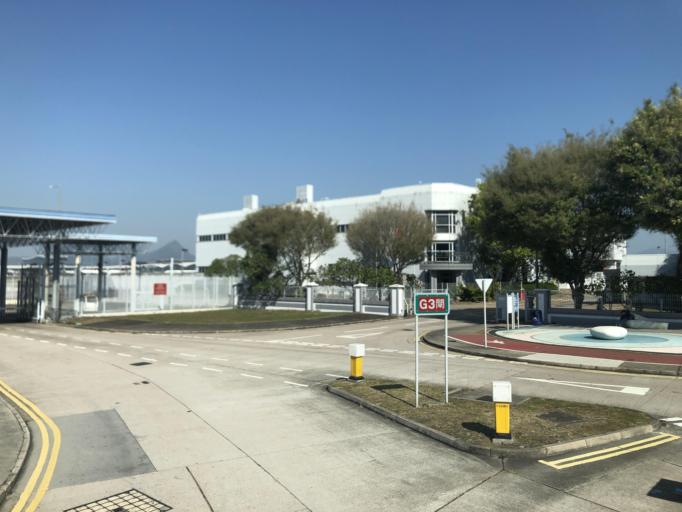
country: HK
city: Tai O
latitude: 22.3028
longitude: 113.9306
